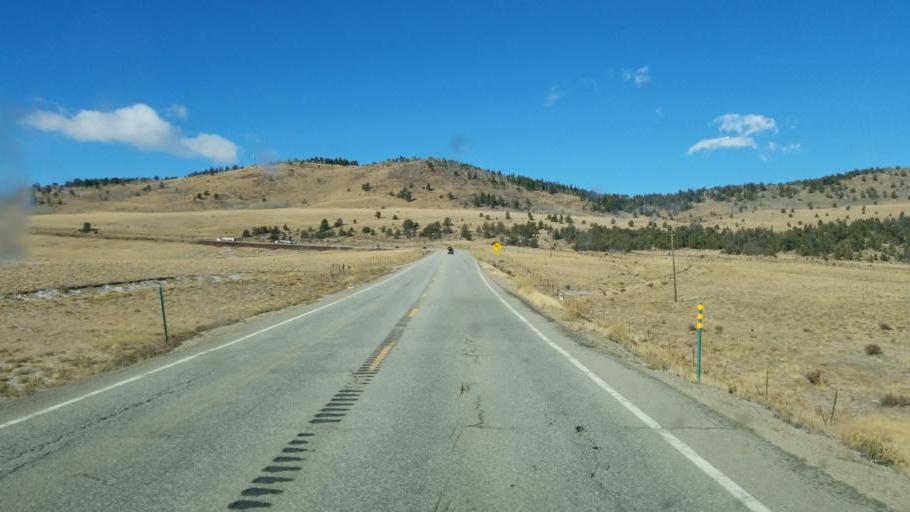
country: US
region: Colorado
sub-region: Park County
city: Fairplay
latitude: 39.2765
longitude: -105.9453
